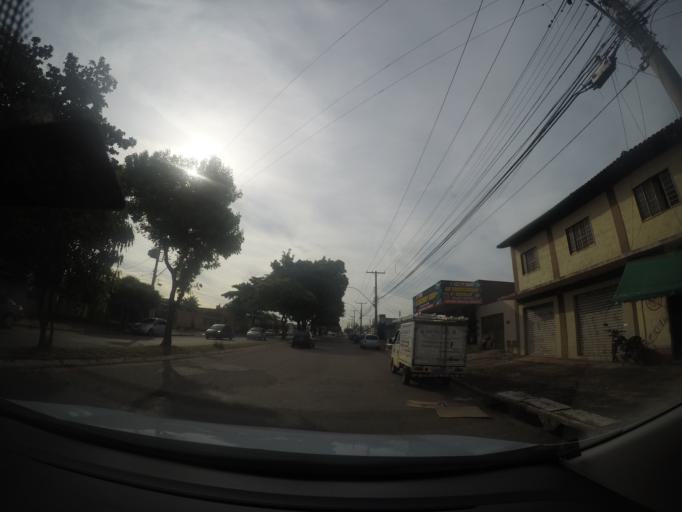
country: BR
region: Goias
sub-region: Goiania
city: Goiania
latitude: -16.6756
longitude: -49.3158
